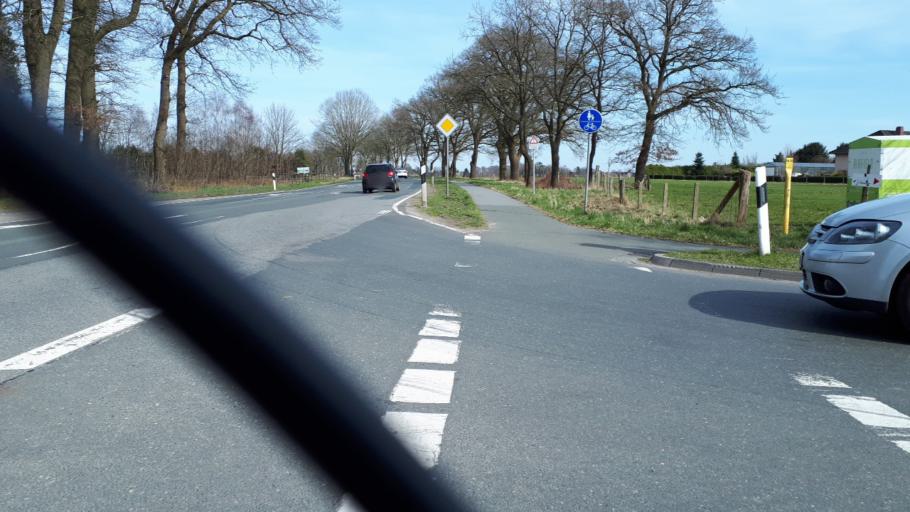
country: DE
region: Lower Saxony
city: Ganderkesee
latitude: 53.0442
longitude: 8.5179
